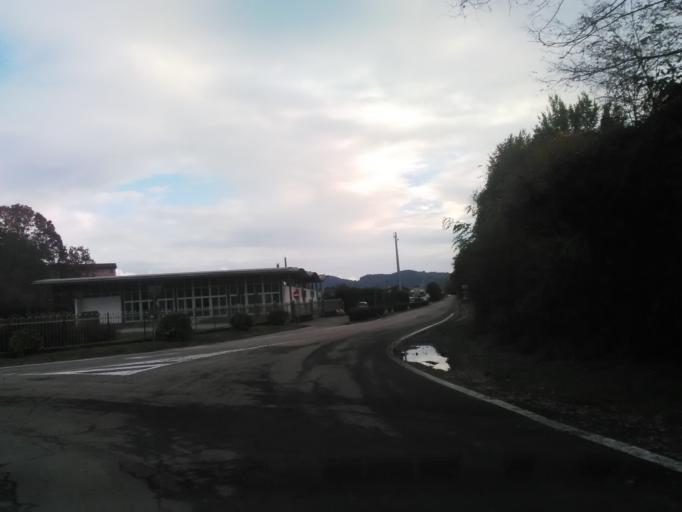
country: IT
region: Piedmont
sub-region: Provincia di Novara
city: Pella
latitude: 45.7836
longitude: 8.3823
